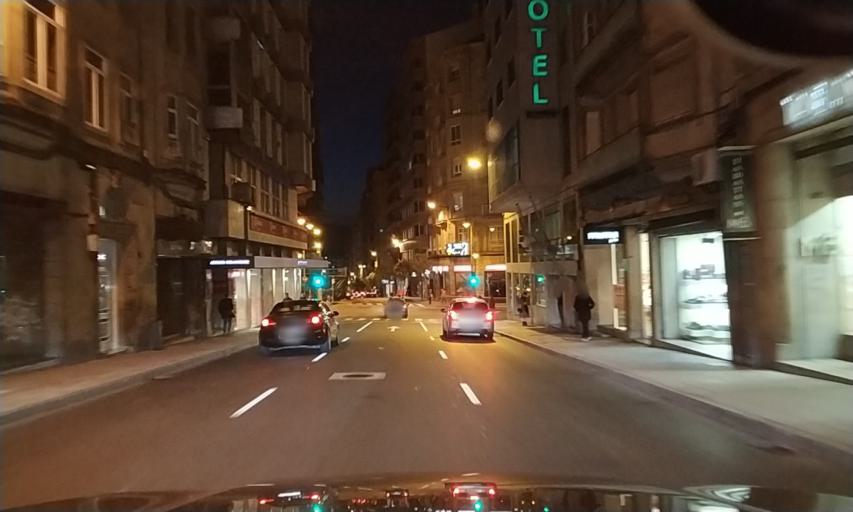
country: ES
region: Galicia
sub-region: Provincia de Ourense
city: Ourense
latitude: 42.3425
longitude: -7.8629
